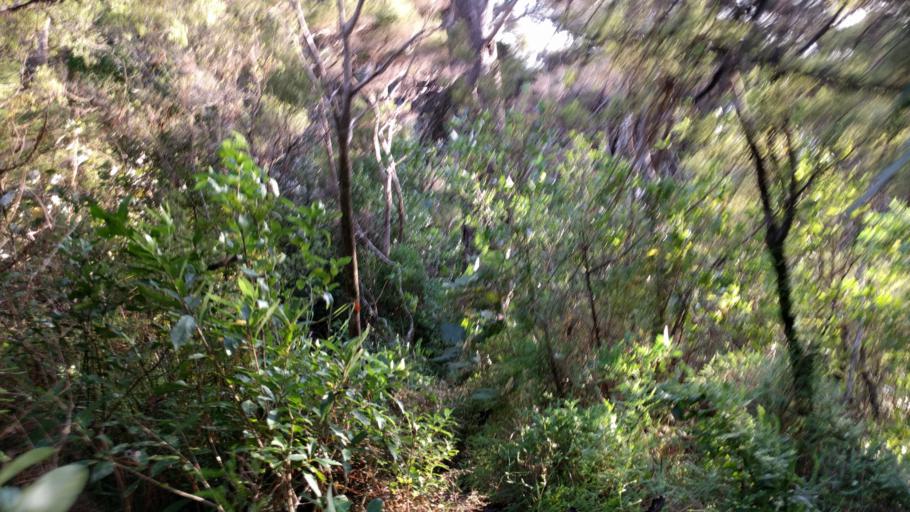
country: NZ
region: Waikato
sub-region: Thames-Coromandel District
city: Thames
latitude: -37.1129
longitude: 175.5275
